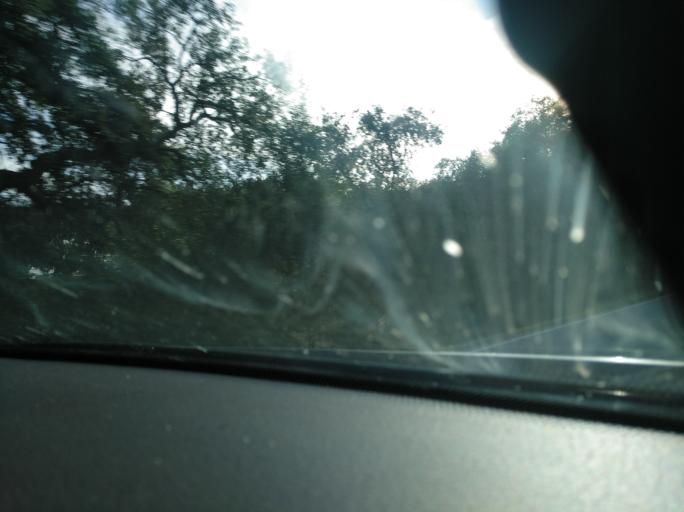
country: PT
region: Portalegre
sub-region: Fronteira
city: Fronteira
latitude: 38.9619
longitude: -7.5971
